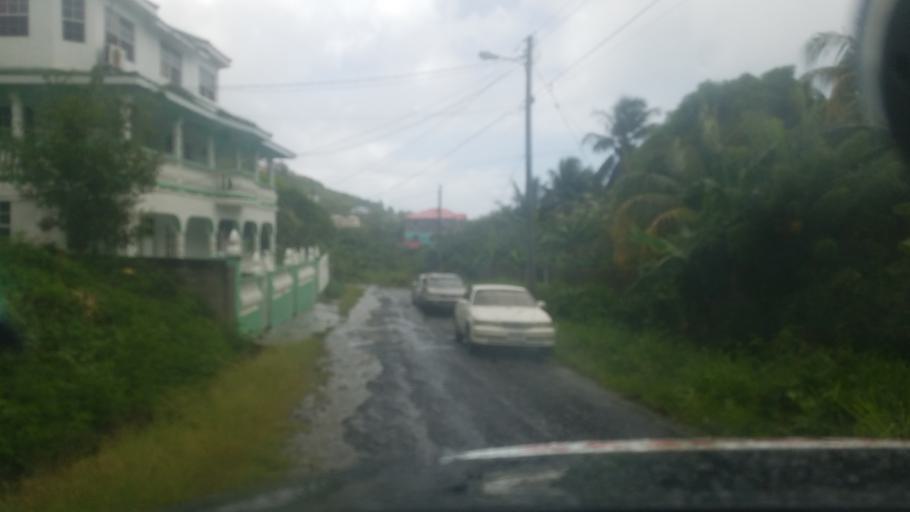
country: LC
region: Laborie Quarter
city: Laborie
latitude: 13.7478
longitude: -60.9695
